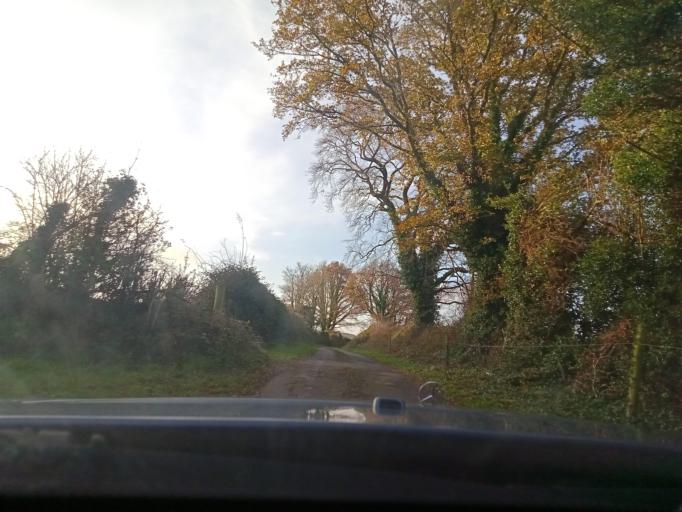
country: IE
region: Leinster
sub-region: Kilkenny
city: Callan
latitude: 52.4847
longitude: -7.4311
